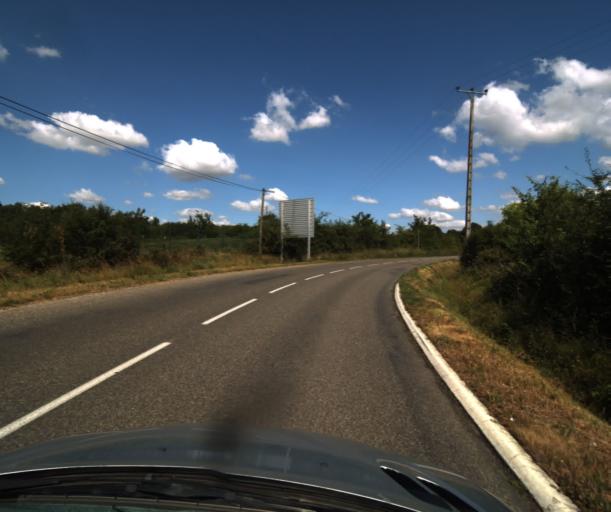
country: FR
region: Midi-Pyrenees
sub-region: Departement du Tarn-et-Garonne
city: Campsas
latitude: 43.9004
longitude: 1.3041
